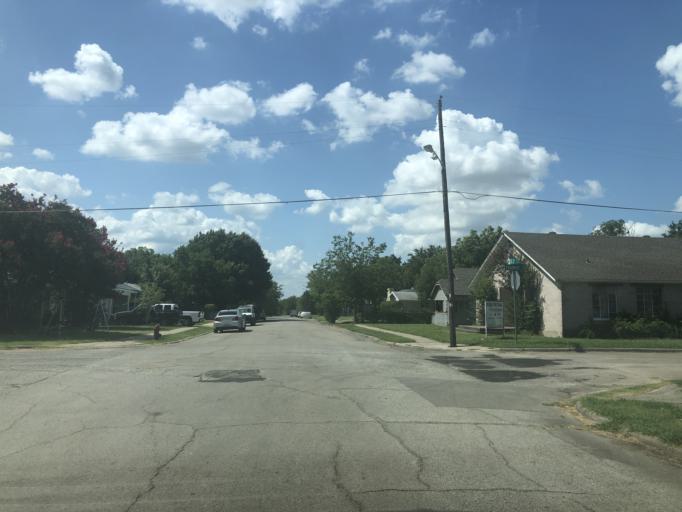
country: US
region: Texas
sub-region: Dallas County
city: Grand Prairie
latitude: 32.7401
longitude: -97.0025
